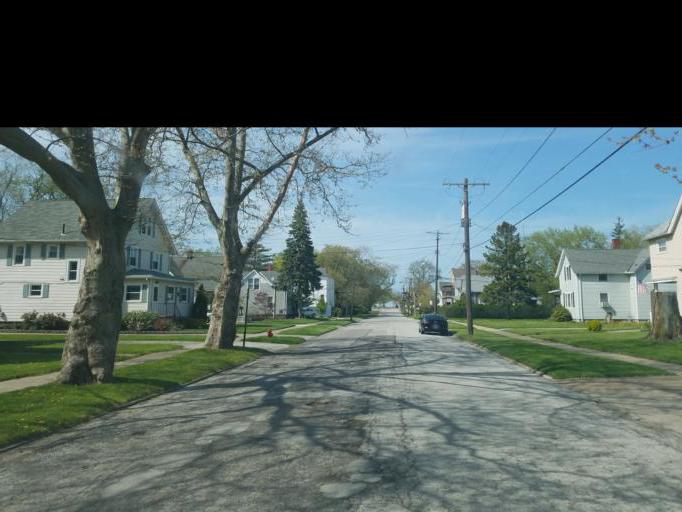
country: US
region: Ohio
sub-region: Lake County
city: Fairport Harbor
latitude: 41.7529
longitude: -81.2755
